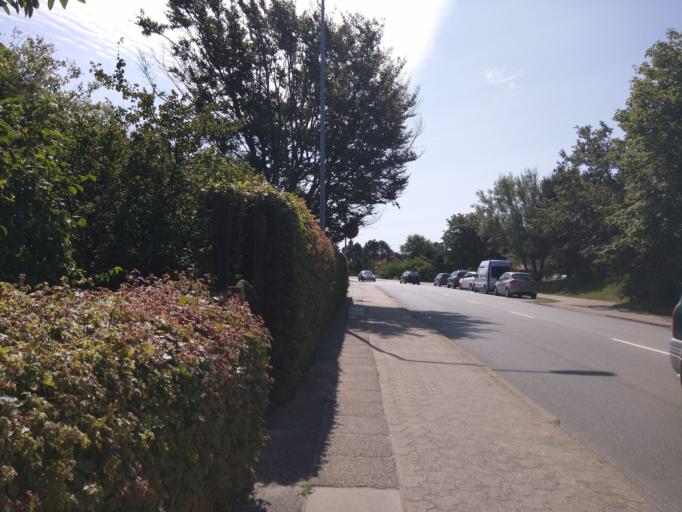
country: DK
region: North Denmark
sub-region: Frederikshavn Kommune
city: Skagen
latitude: 57.7212
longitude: 10.5760
